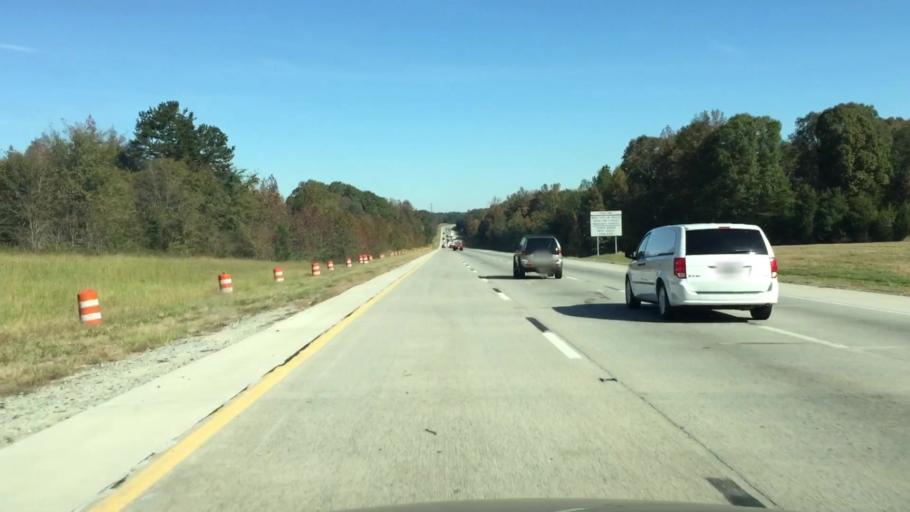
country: US
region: North Carolina
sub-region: Guilford County
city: Jamestown
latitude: 35.9664
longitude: -79.8926
